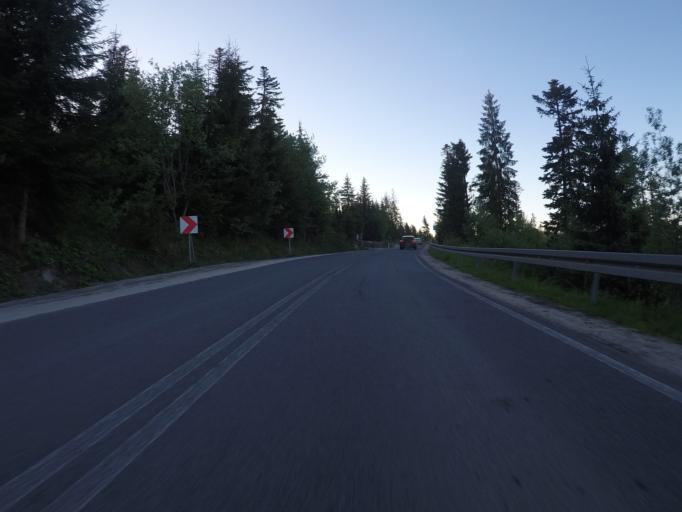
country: PL
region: Lesser Poland Voivodeship
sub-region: Powiat tatrzanski
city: Bukowina Tatrzanska
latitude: 49.2840
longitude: 20.1132
